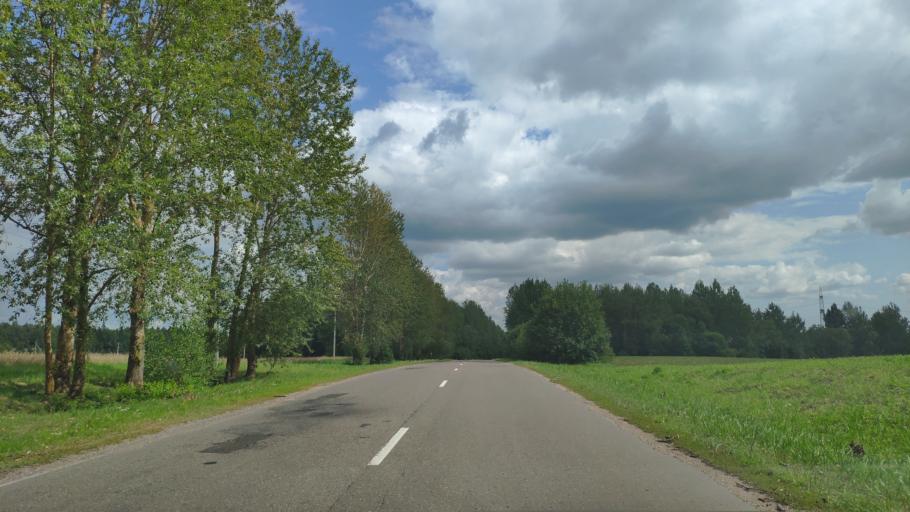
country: BY
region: Minsk
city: Khatsyezhyna
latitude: 53.8787
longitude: 27.2860
